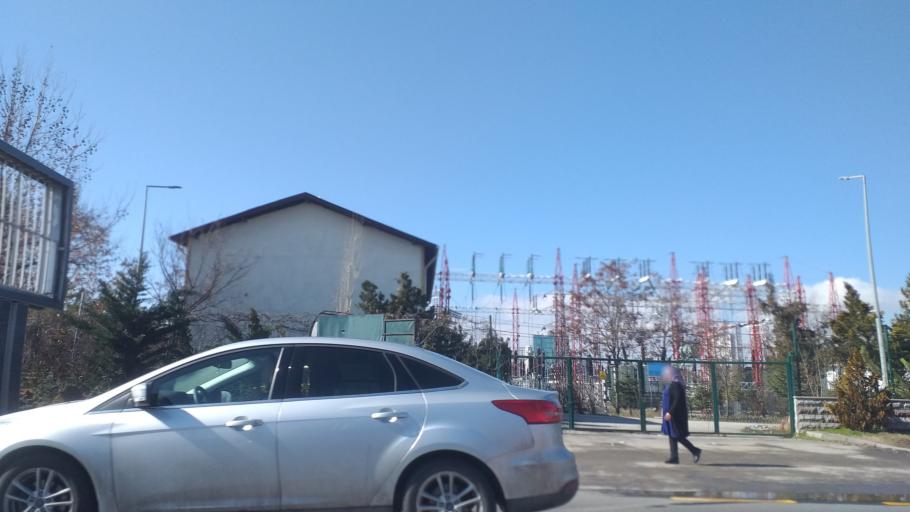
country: TR
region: Ankara
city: Ankara
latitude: 39.9149
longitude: 32.8141
